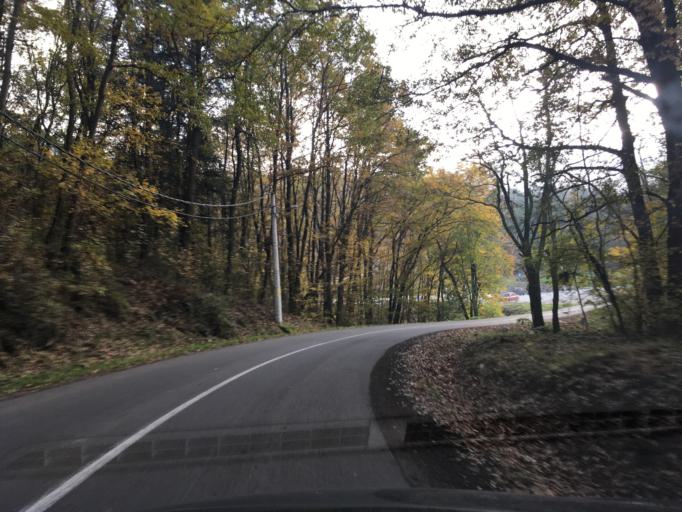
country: RS
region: Central Serbia
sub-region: Belgrade
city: Sopot
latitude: 44.4748
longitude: 20.5672
